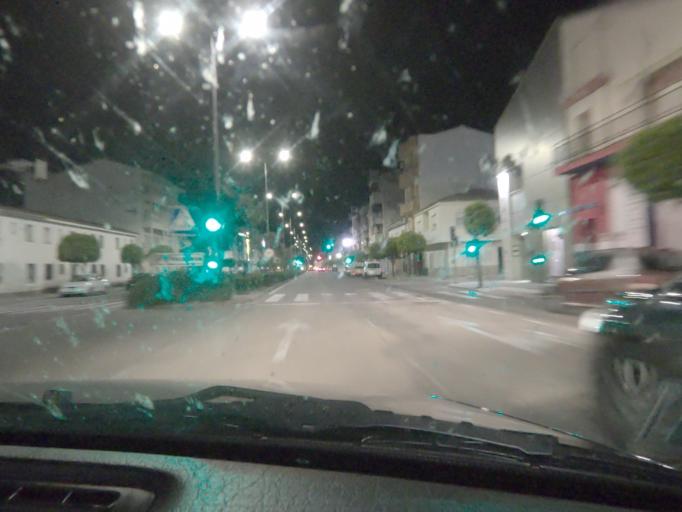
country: ES
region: Extremadura
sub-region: Provincia de Caceres
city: Moraleja
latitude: 40.0673
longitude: -6.6547
